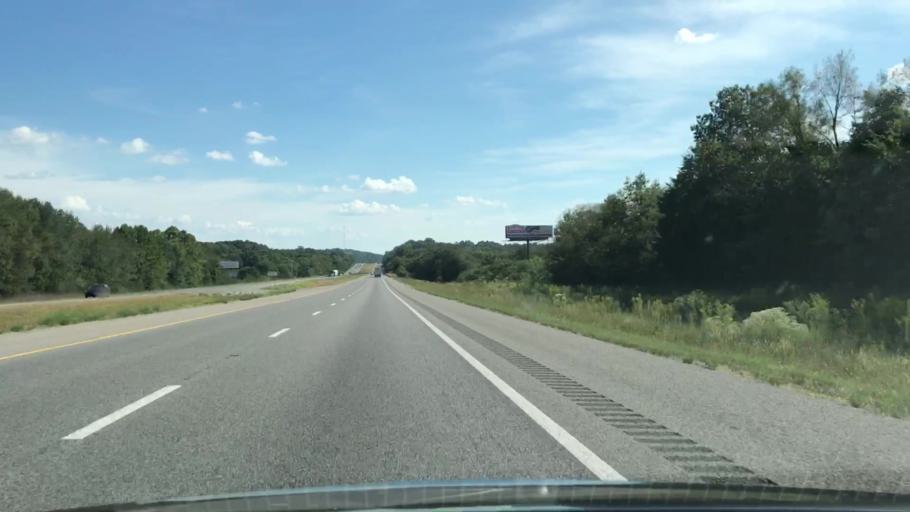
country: US
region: Alabama
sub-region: Limestone County
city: Ardmore
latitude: 35.0570
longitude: -86.8813
